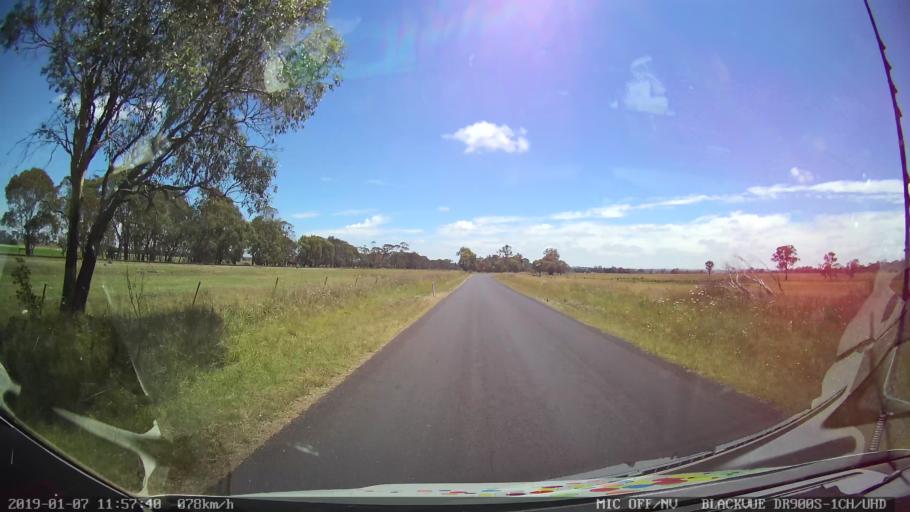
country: AU
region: New South Wales
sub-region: Guyra
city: Guyra
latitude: -30.2617
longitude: 151.6658
